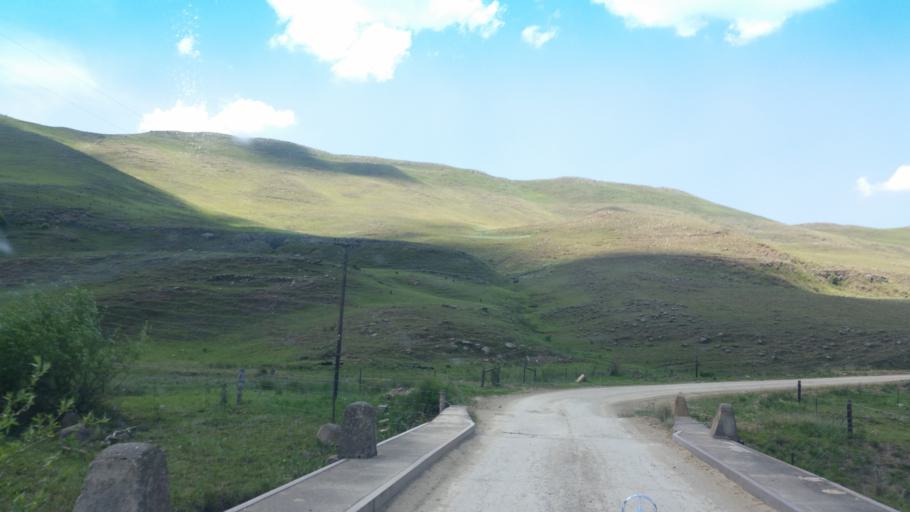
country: ZA
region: KwaZulu-Natal
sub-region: uMgungundlovu District Municipality
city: Impendle
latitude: -29.4464
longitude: 29.7518
